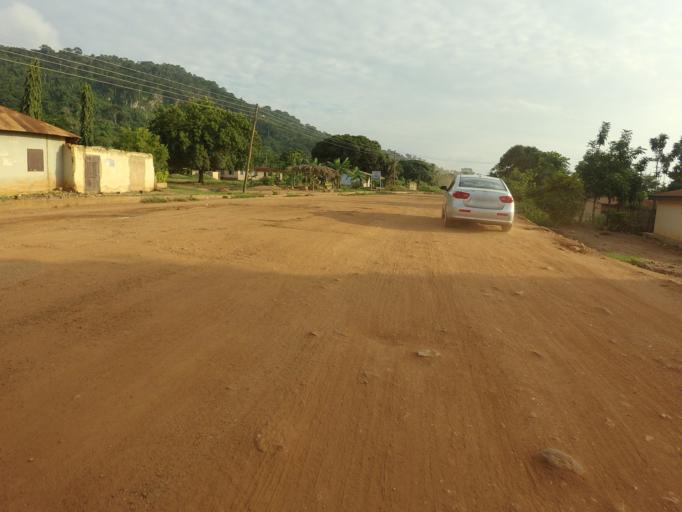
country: TG
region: Plateaux
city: Kpalime
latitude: 6.9189
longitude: 0.4601
